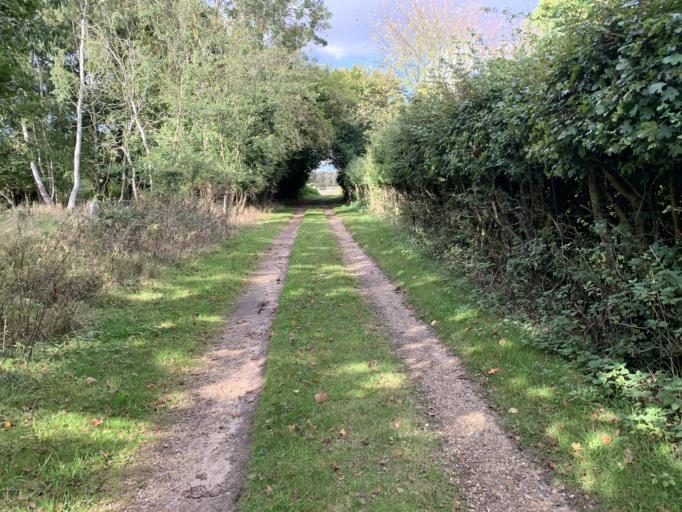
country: GB
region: England
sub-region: Suffolk
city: Aldeburgh
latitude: 52.1242
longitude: 1.5304
